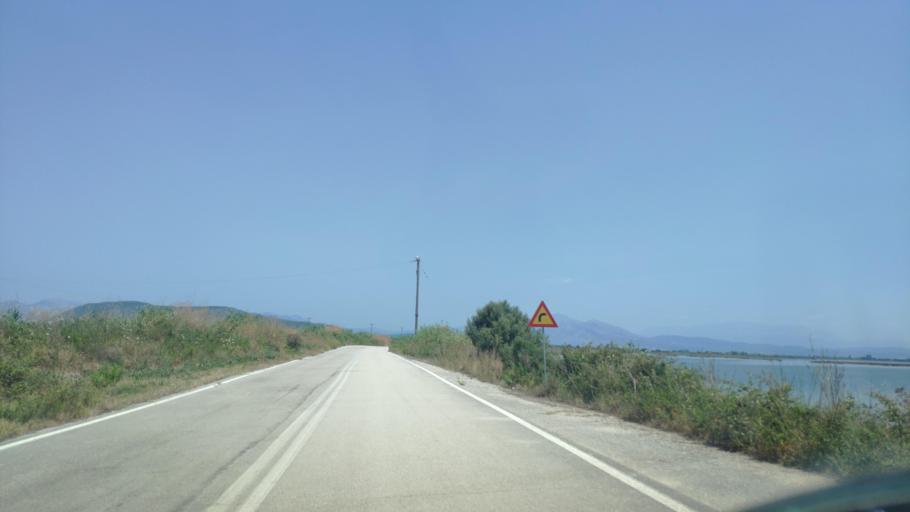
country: GR
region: Epirus
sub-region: Nomos Artas
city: Aneza
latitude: 39.0418
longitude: 20.8600
